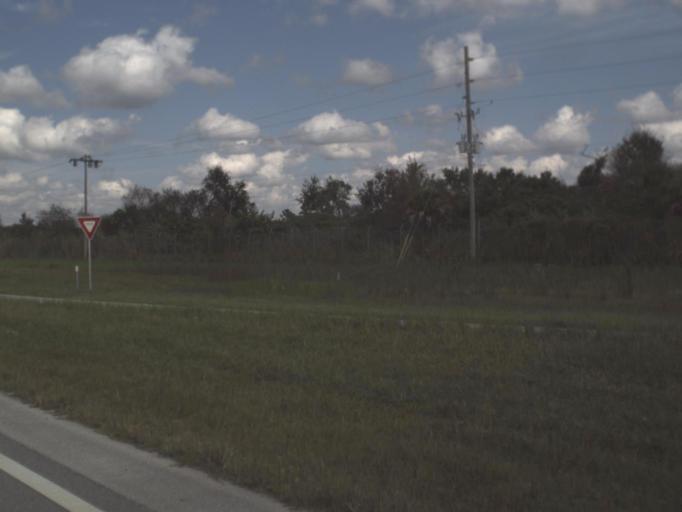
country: US
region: Florida
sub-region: Collier County
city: Immokalee
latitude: 26.1585
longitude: -81.3451
